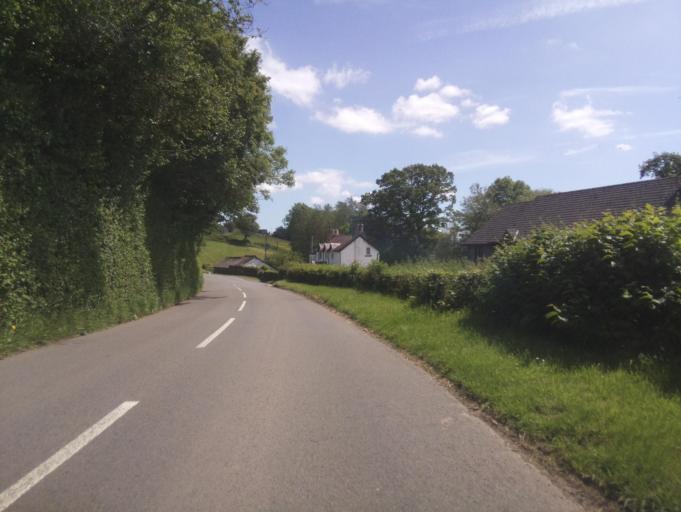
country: GB
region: England
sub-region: Herefordshire
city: Llanrothal
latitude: 51.8419
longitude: -2.7758
